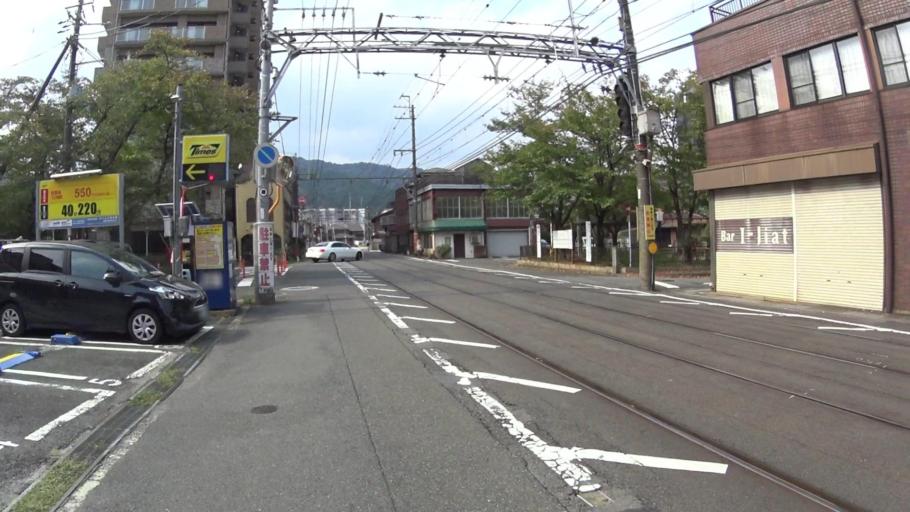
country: JP
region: Osaka
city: Izumiotsu
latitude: 34.5239
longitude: 135.3565
